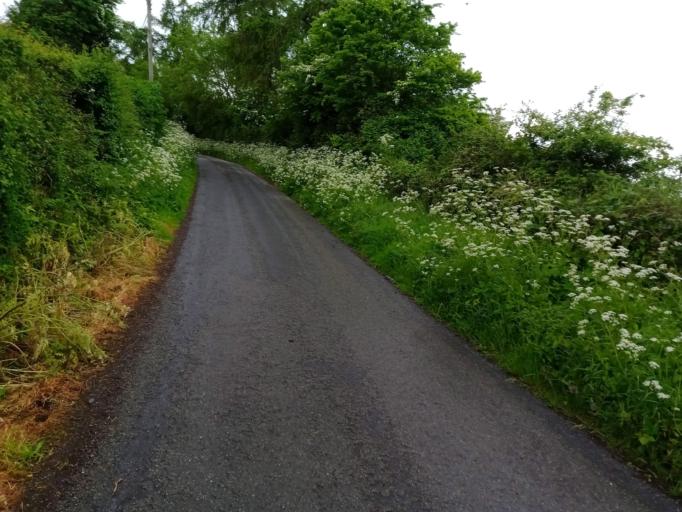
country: IE
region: Leinster
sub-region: Kilkenny
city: Thomastown
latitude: 52.5177
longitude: -7.1346
